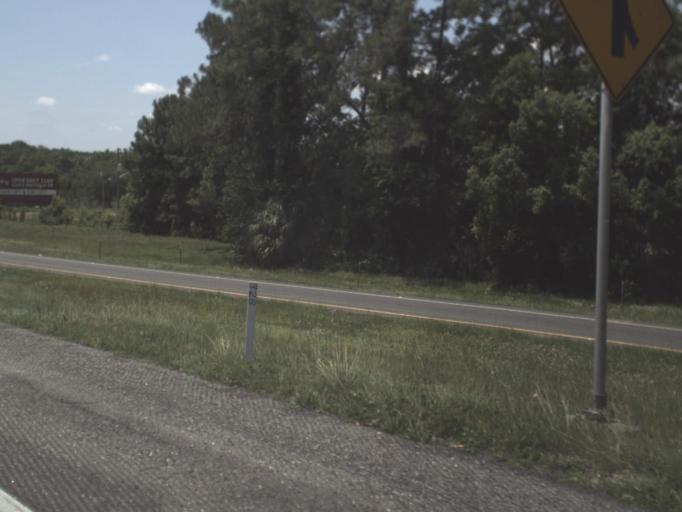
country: US
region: Florida
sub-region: Nassau County
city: Yulee
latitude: 30.5152
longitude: -81.6350
